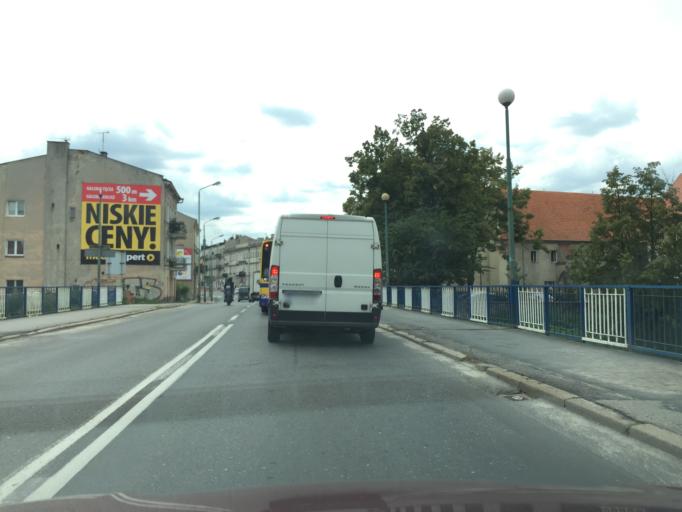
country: PL
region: Greater Poland Voivodeship
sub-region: Kalisz
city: Kalisz
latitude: 51.7670
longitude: 18.0954
